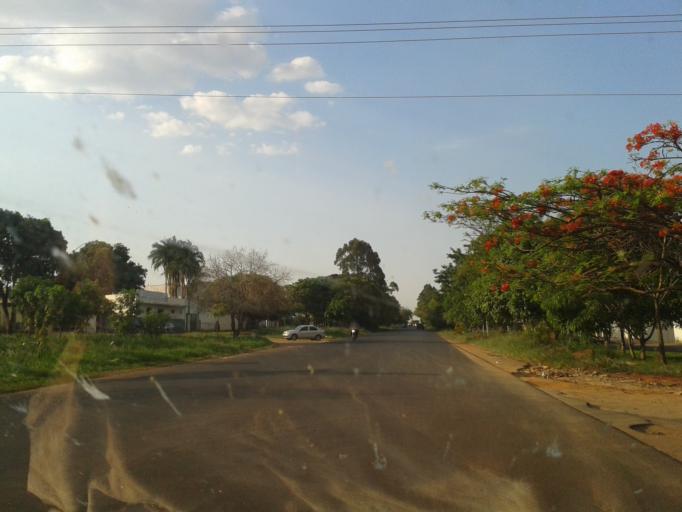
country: BR
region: Minas Gerais
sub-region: Uberlandia
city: Uberlandia
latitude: -18.9468
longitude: -48.3071
